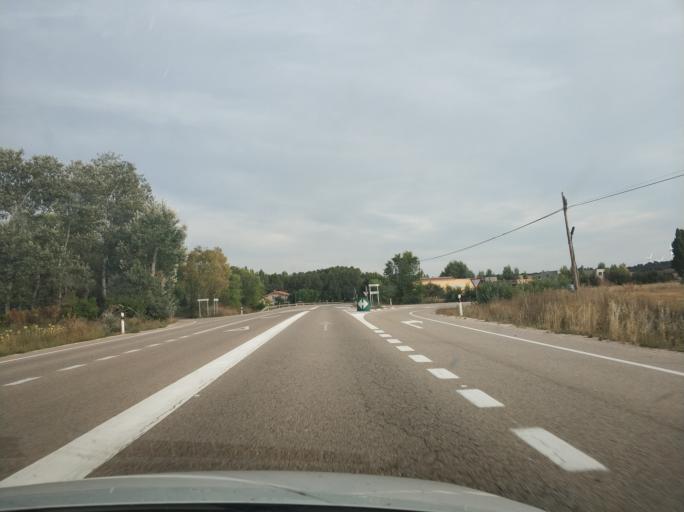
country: ES
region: Castille and Leon
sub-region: Provincia de Burgos
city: Revillarruz
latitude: 42.2370
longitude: -3.6690
